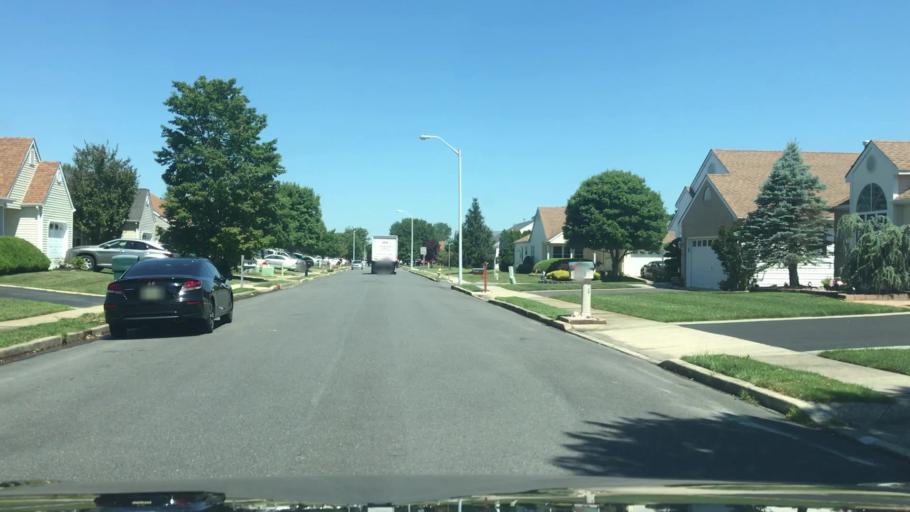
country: US
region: New Jersey
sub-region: Ocean County
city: Holiday City South
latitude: 39.9434
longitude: -74.2386
